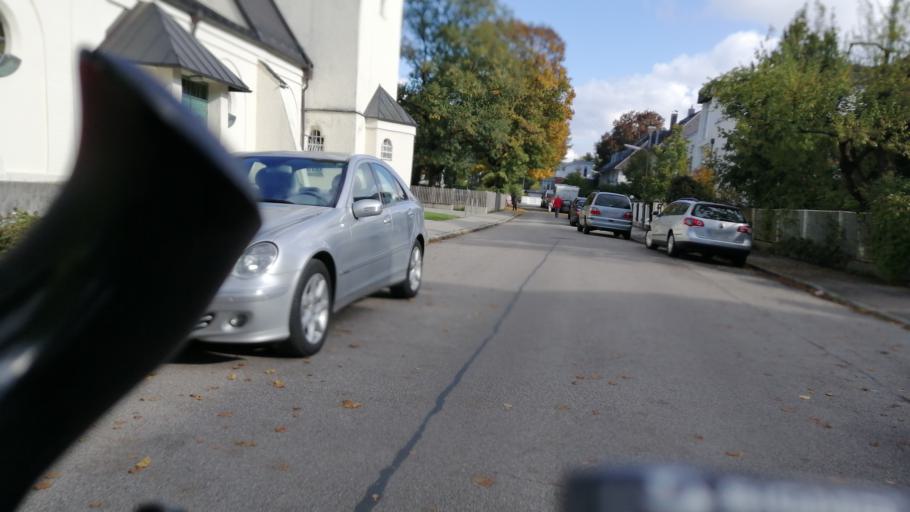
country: DE
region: Bavaria
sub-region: Upper Bavaria
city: Neuried
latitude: 48.1132
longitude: 11.4812
